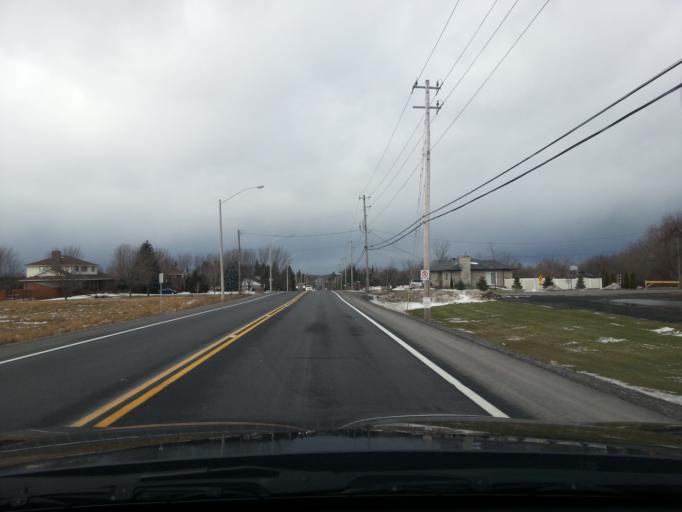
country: CA
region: Ontario
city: Ottawa
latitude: 45.2972
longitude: -75.6103
